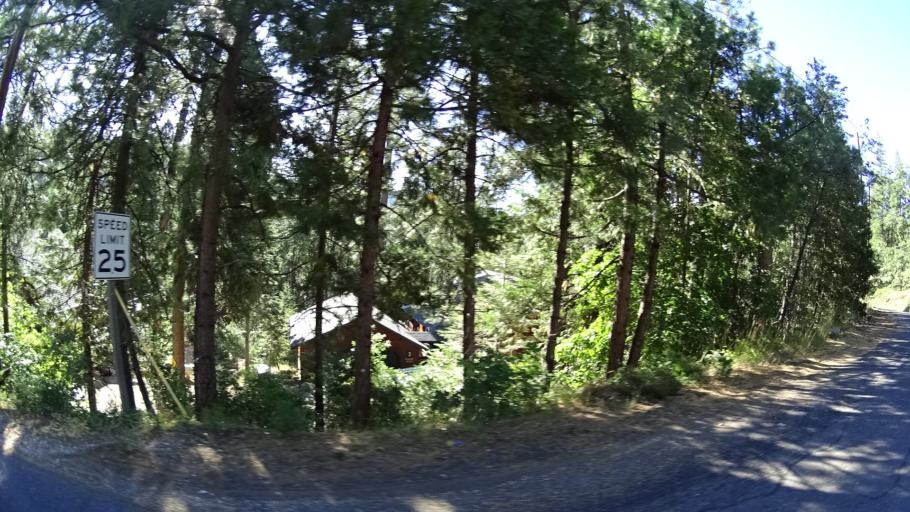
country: US
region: California
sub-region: Calaveras County
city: Arnold
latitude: 38.2634
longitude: -120.3329
